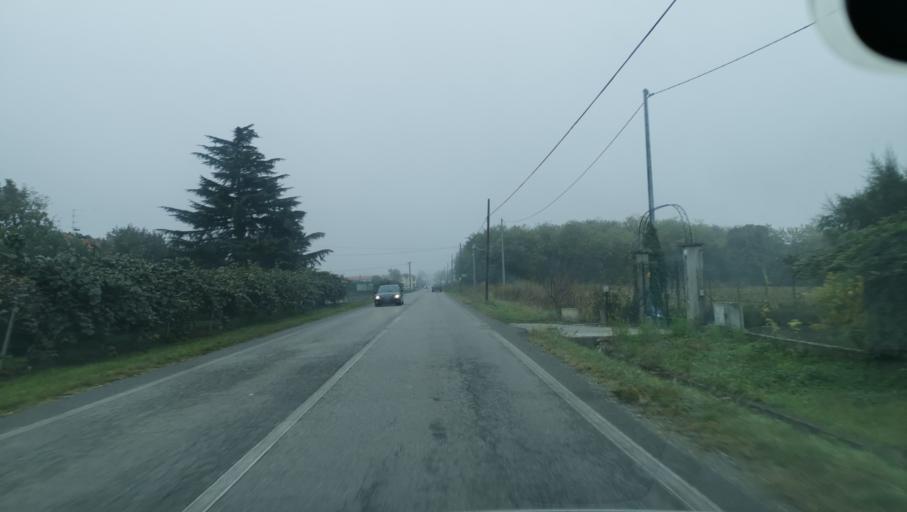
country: IT
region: Piedmont
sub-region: Provincia di Biella
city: Cavaglia
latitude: 45.3929
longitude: 8.0885
